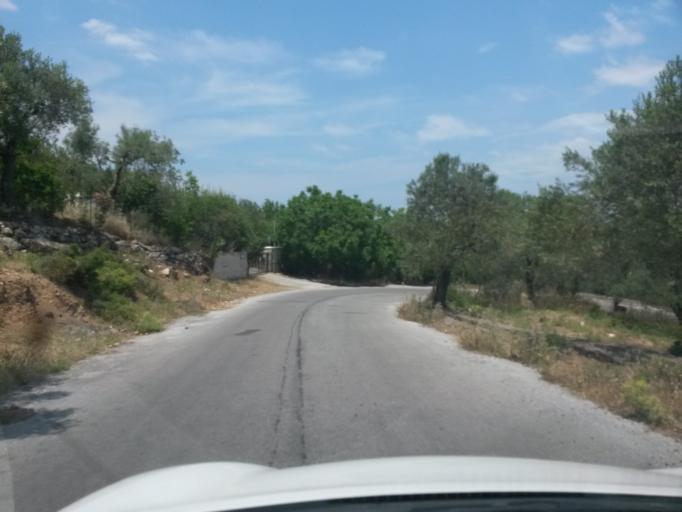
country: GR
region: North Aegean
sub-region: Nomos Lesvou
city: Pamfylla
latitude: 39.1775
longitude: 26.4817
